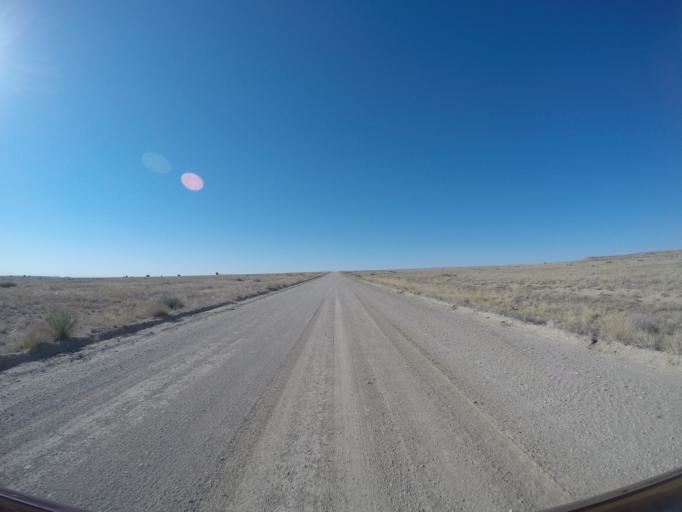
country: US
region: Colorado
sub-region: Otero County
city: La Junta
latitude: 37.7870
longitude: -103.5296
